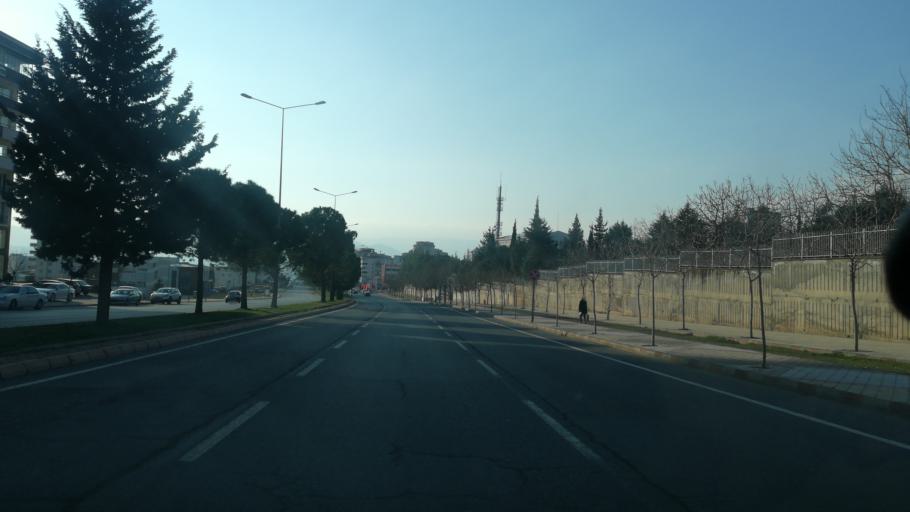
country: TR
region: Kahramanmaras
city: Kahramanmaras
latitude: 37.5999
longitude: 36.8352
